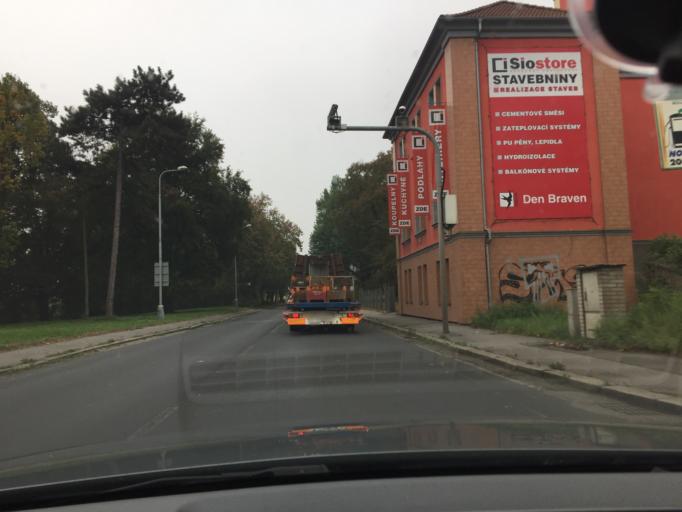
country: CZ
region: Ustecky
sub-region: Okres Usti nad Labem
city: Usti nad Labem
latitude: 50.6526
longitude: 14.0410
